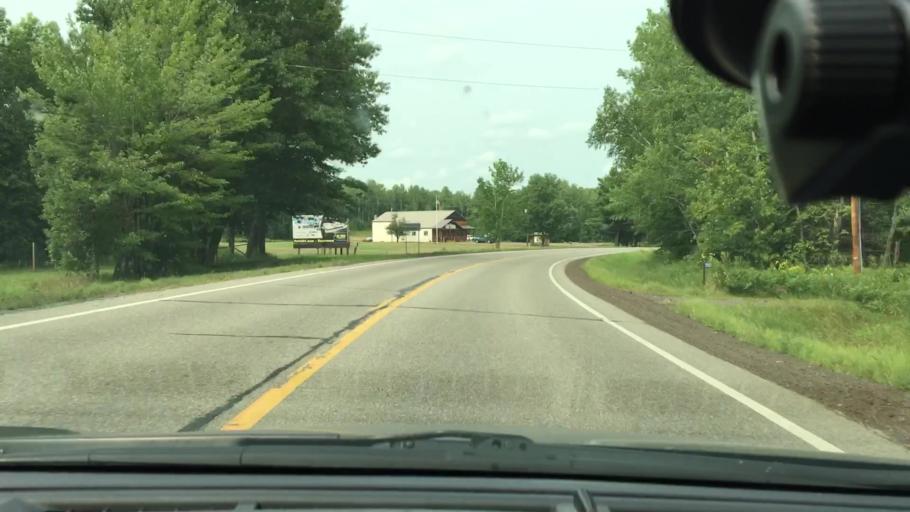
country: US
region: Minnesota
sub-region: Crow Wing County
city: Cross Lake
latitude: 46.8242
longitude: -93.9483
